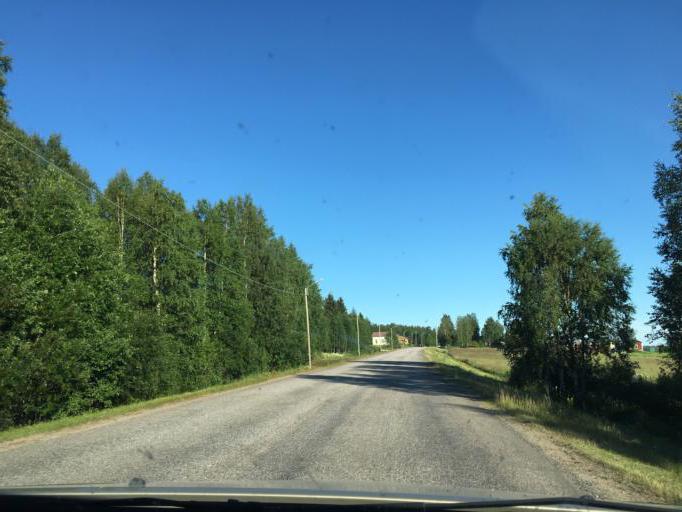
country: SE
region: Norrbotten
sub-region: Kalix Kommun
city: Rolfs
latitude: 65.9251
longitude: 22.9048
